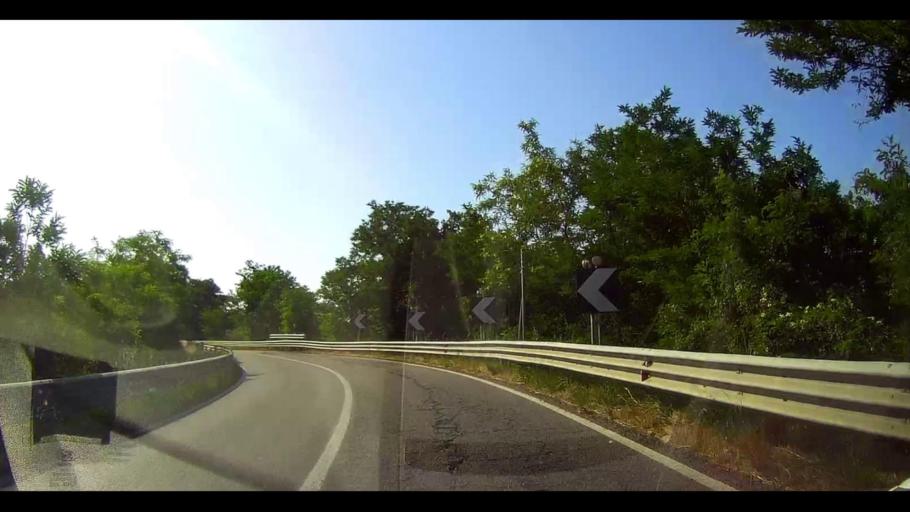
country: IT
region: Calabria
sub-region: Provincia di Cosenza
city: Cariati
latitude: 39.4830
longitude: 16.9768
